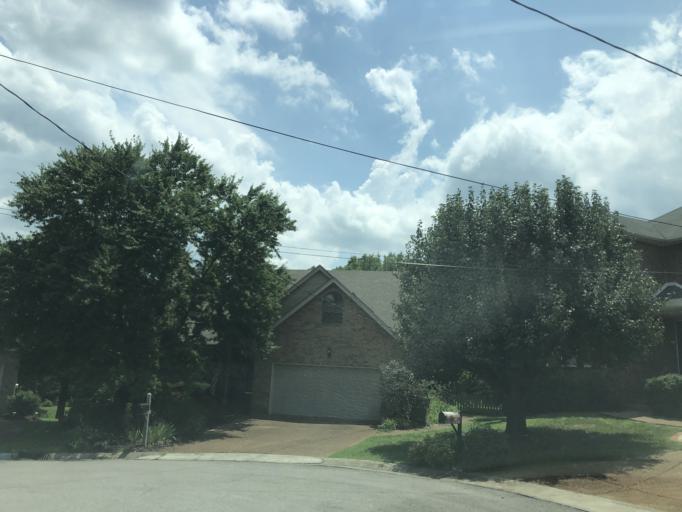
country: US
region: Tennessee
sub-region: Williamson County
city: Brentwood Estates
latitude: 36.0177
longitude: -86.7274
